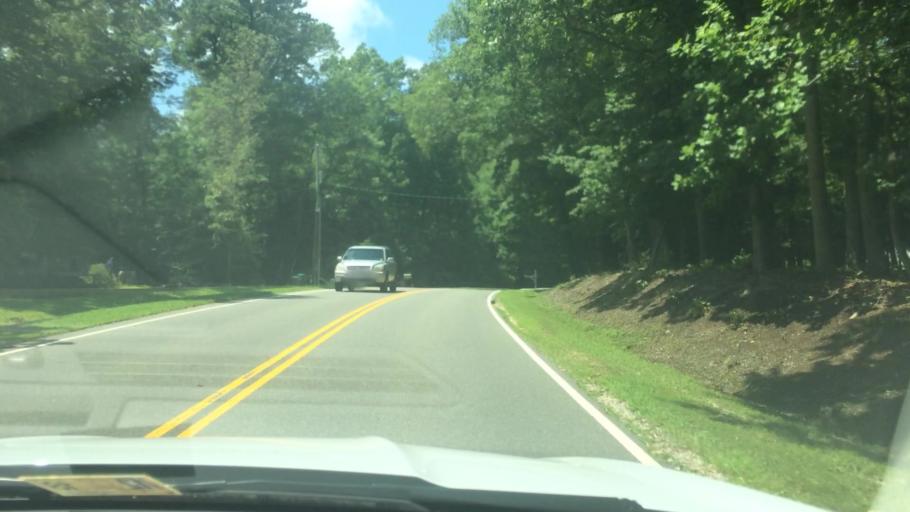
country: US
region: Virginia
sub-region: James City County
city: Williamsburg
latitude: 37.2796
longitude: -76.7964
